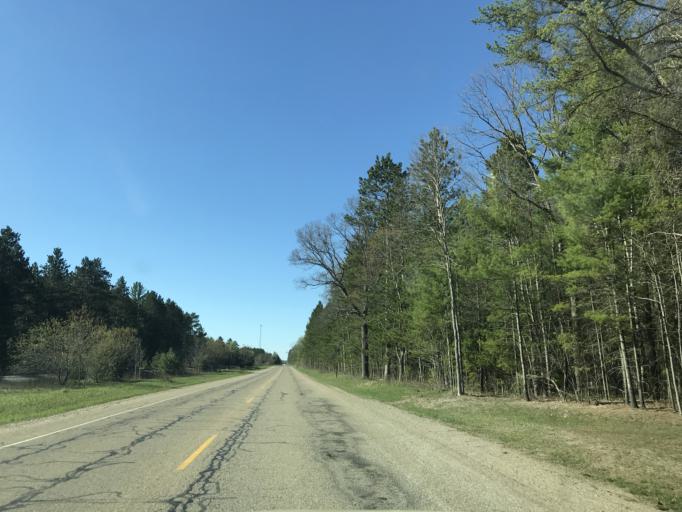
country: US
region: Michigan
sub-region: Crawford County
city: Grayling
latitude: 44.7281
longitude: -84.7482
